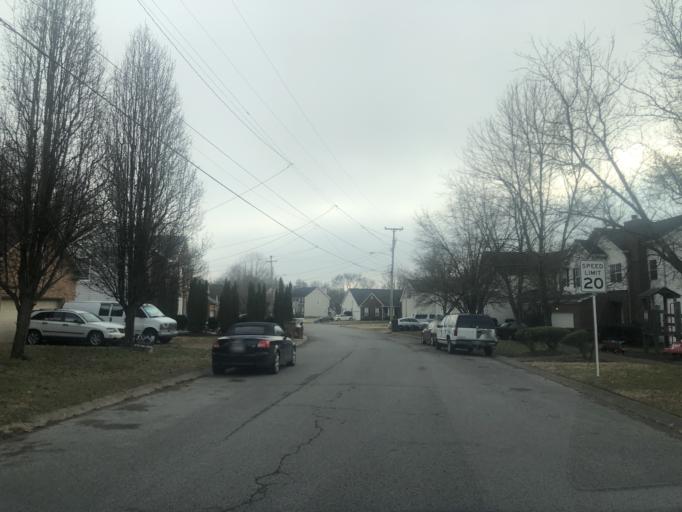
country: US
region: Tennessee
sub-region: Rutherford County
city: La Vergne
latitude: 36.0734
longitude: -86.6549
